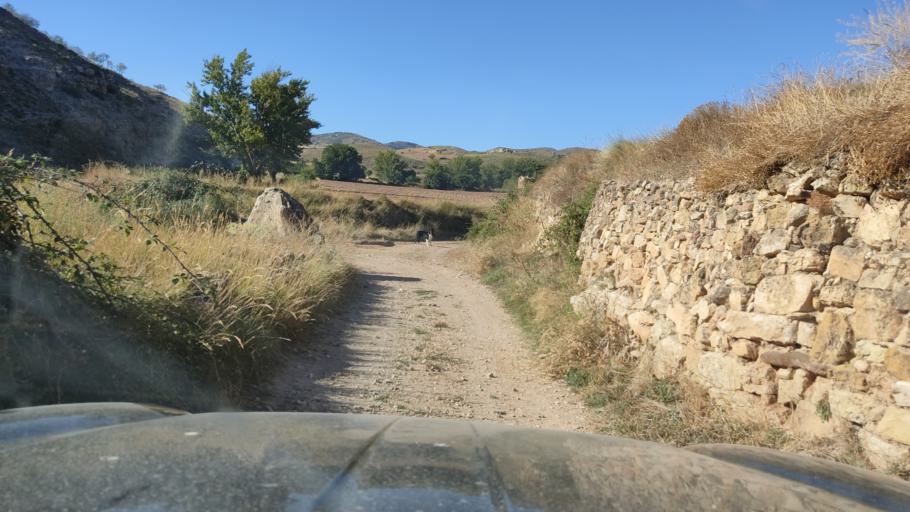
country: ES
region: Aragon
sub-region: Provincia de Teruel
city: Monforte de Moyuela
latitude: 41.0457
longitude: -1.0134
